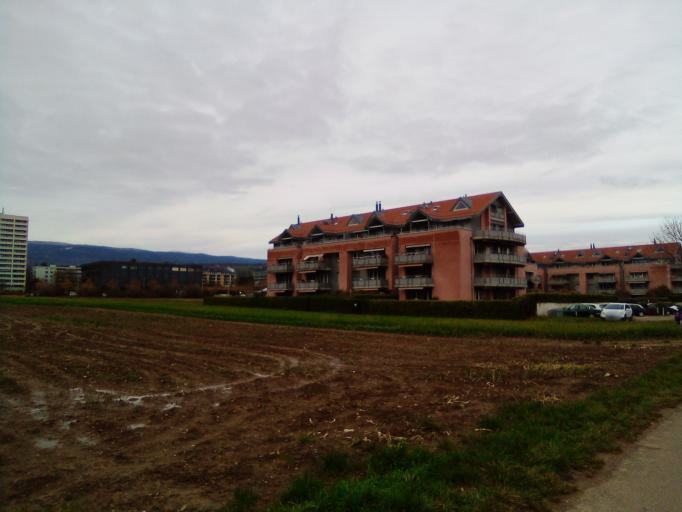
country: CH
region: Vaud
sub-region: Nyon District
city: Gland
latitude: 46.4193
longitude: 6.2586
